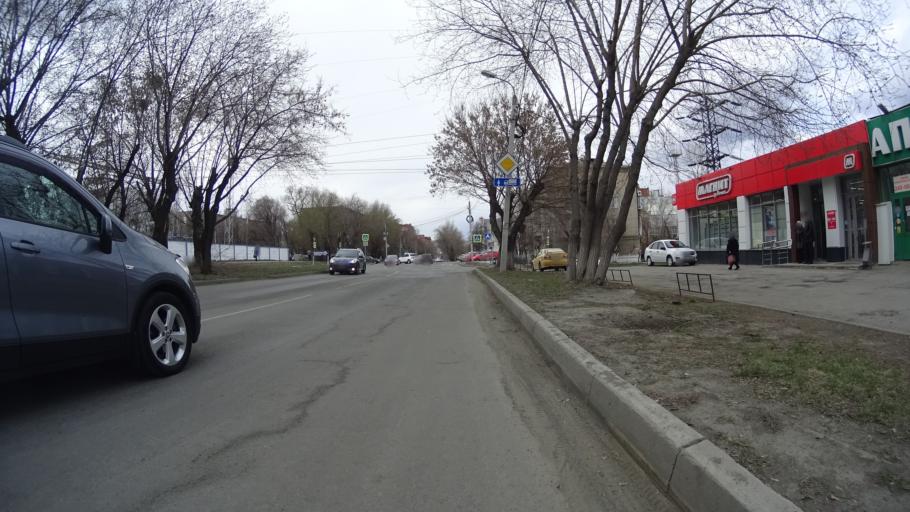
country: RU
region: Chelyabinsk
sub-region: Gorod Chelyabinsk
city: Chelyabinsk
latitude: 55.1633
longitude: 61.4216
